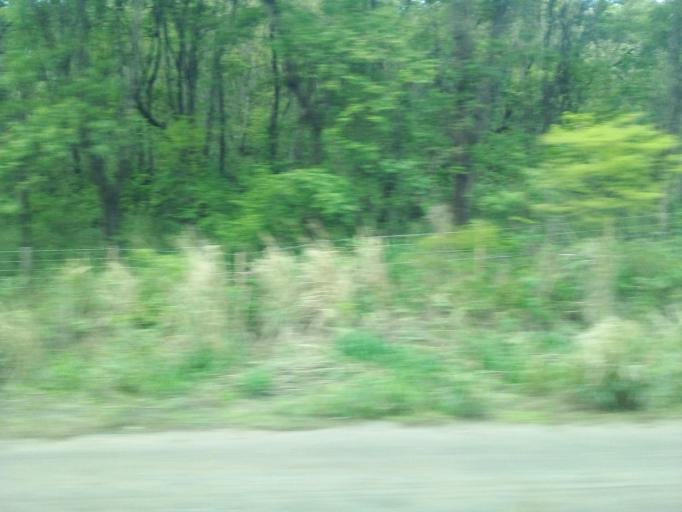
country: BR
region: Minas Gerais
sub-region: Conselheiro Pena
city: Conselheiro Pena
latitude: -19.1398
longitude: -41.4809
